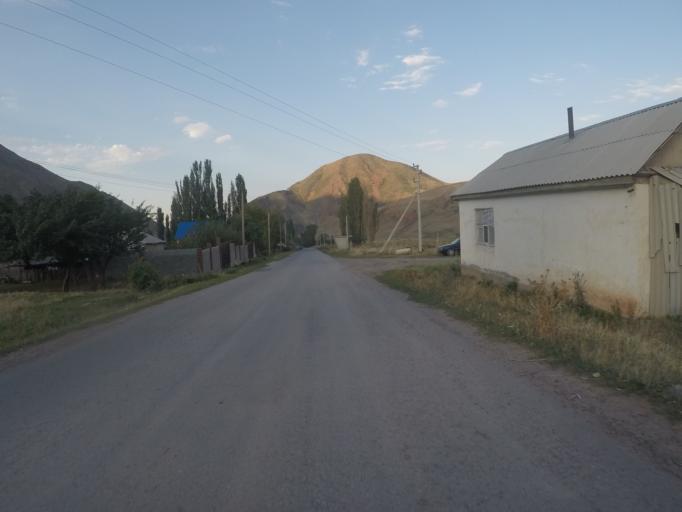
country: KG
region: Chuy
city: Bishkek
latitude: 42.6717
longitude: 74.6489
